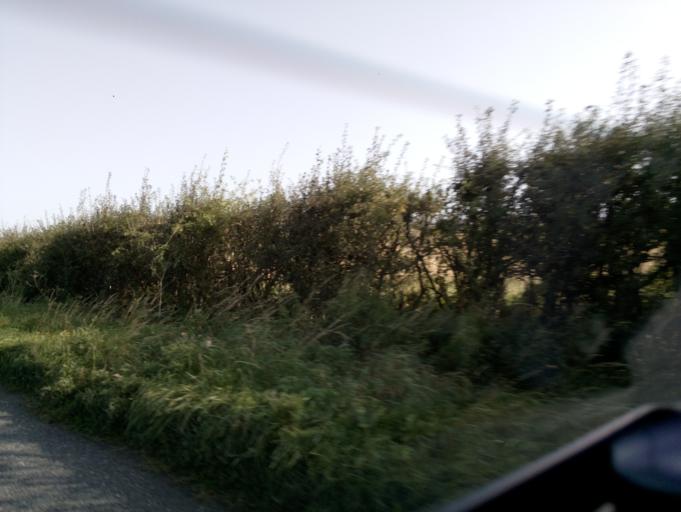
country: GB
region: England
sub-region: Gloucestershire
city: Tewkesbury
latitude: 51.9589
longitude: -2.1667
